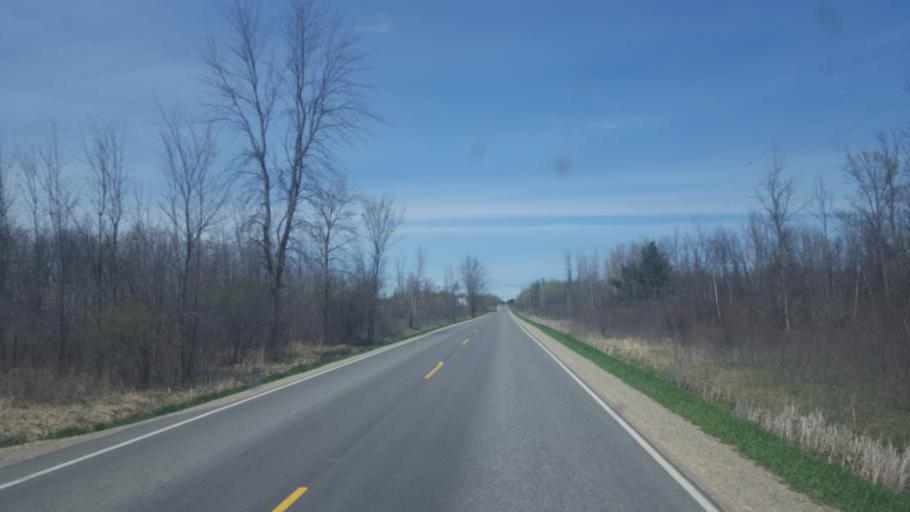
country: US
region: Michigan
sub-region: Gladwin County
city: Beaverton
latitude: 43.8926
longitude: -84.5855
